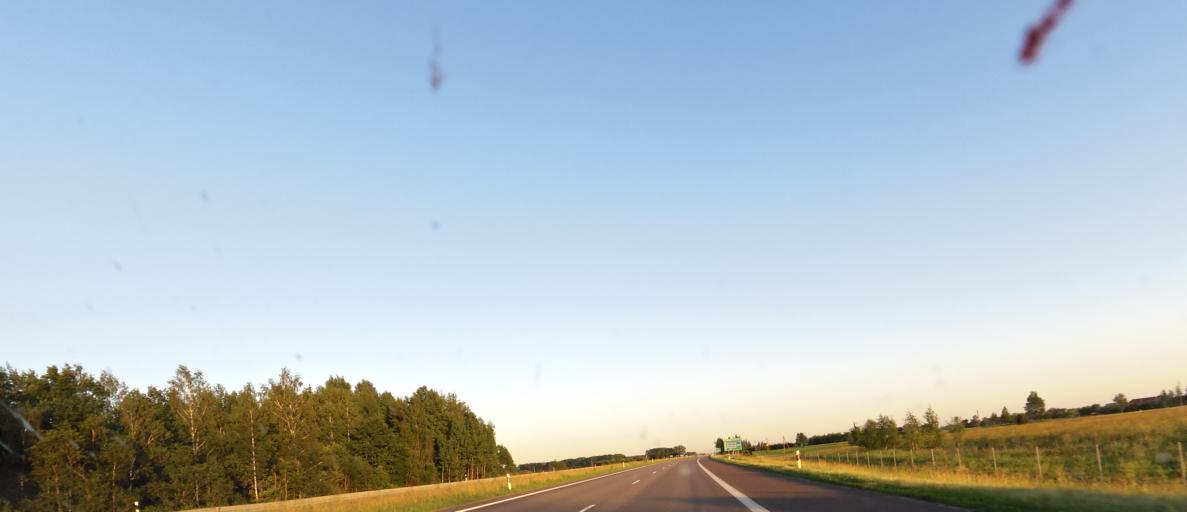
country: LT
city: Sirvintos
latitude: 55.0742
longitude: 24.8810
